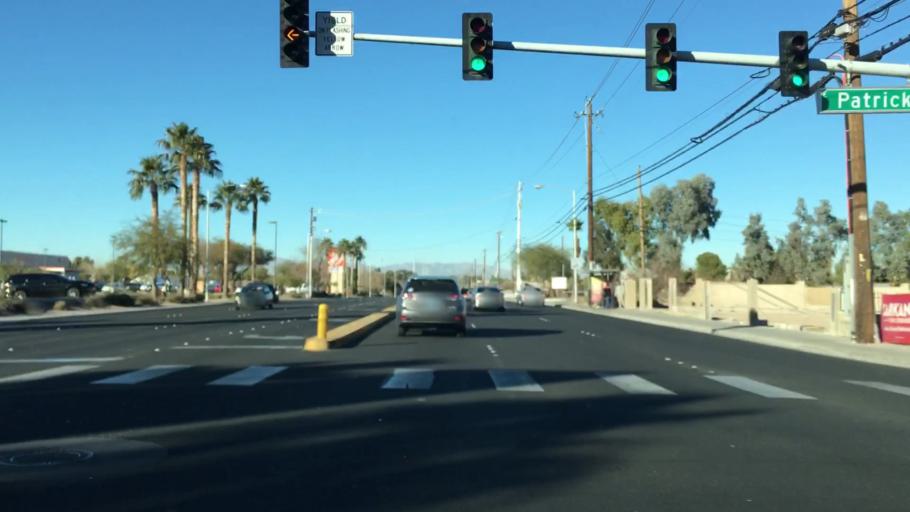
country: US
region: Nevada
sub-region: Clark County
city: Whitney
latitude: 36.0792
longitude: -115.1009
